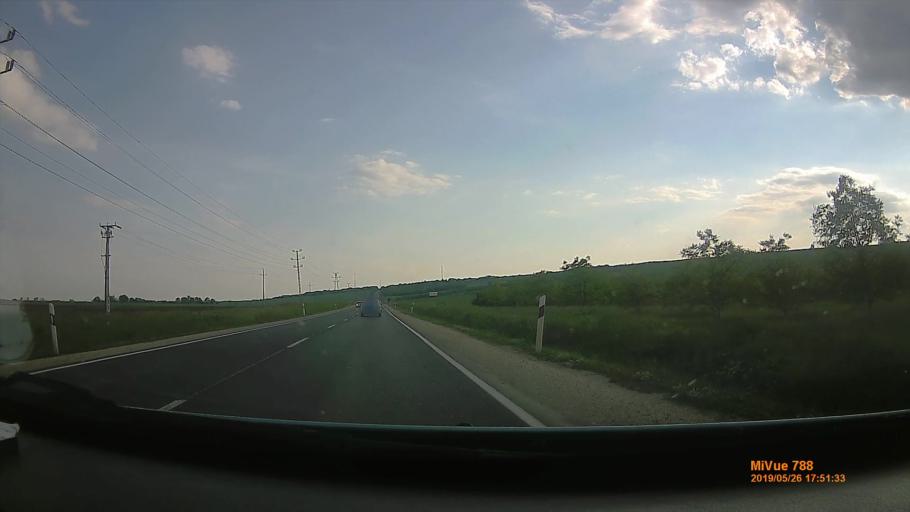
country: HU
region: Borsod-Abauj-Zemplen
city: Szikszo
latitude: 48.1736
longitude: 20.9137
